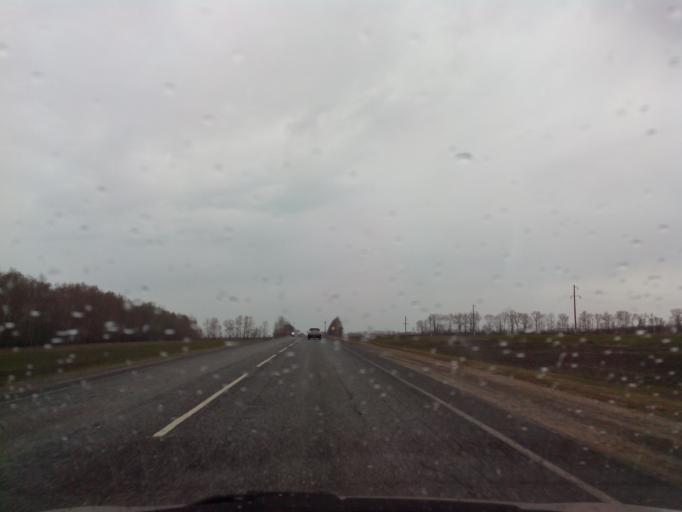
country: RU
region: Tambov
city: Pervomayskiy
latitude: 53.1356
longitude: 40.3802
